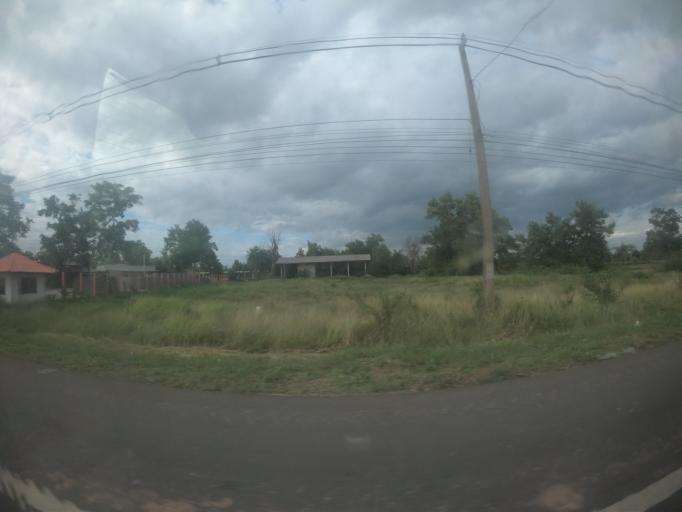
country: TH
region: Surin
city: Kap Choeng
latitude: 14.5361
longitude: 103.5252
